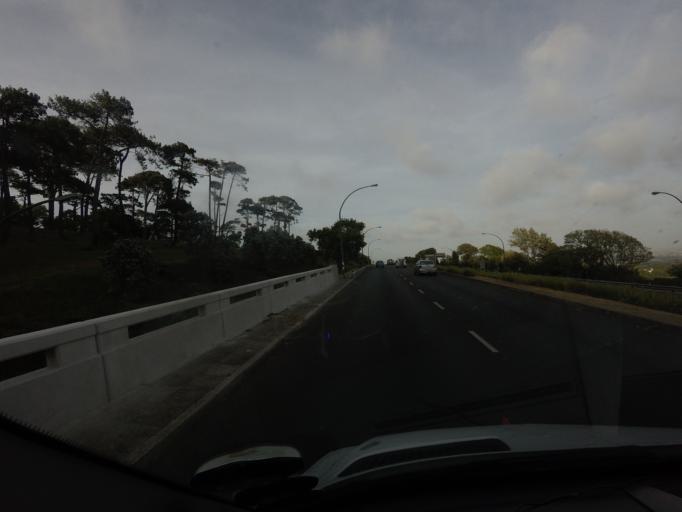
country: ZA
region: Western Cape
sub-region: City of Cape Town
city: Newlands
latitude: -33.9965
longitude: 18.4528
